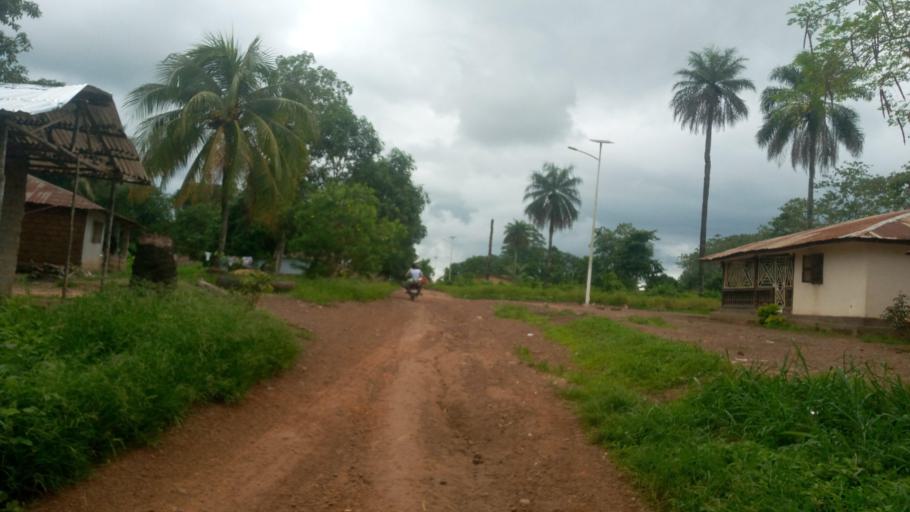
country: SL
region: Southern Province
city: Mogbwemo
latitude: 7.5988
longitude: -12.1749
